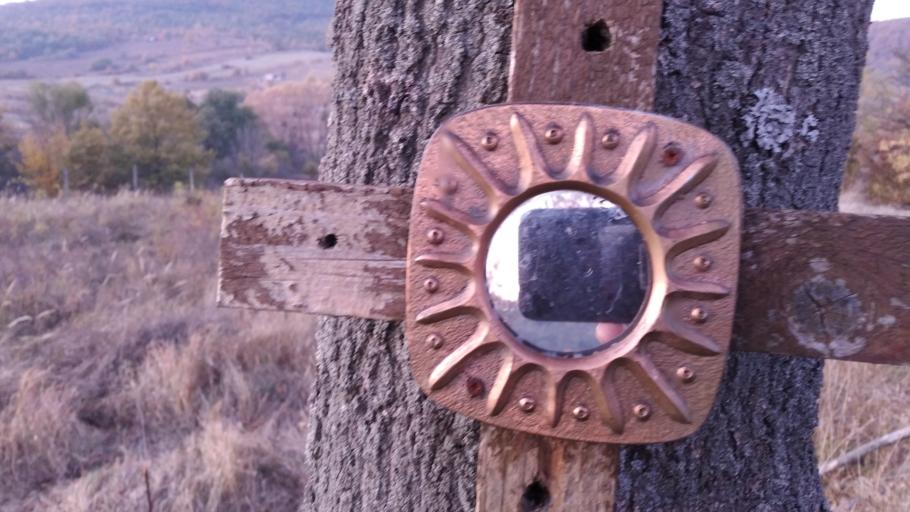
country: HU
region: Pest
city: Visegrad
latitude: 47.7291
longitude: 18.9824
